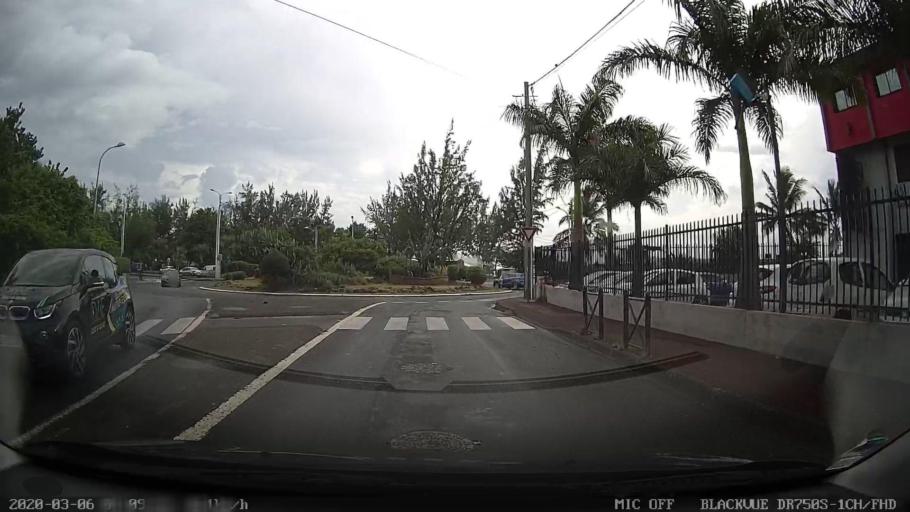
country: RE
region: Reunion
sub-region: Reunion
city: Saint-Pierre
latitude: -21.3382
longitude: 55.4587
